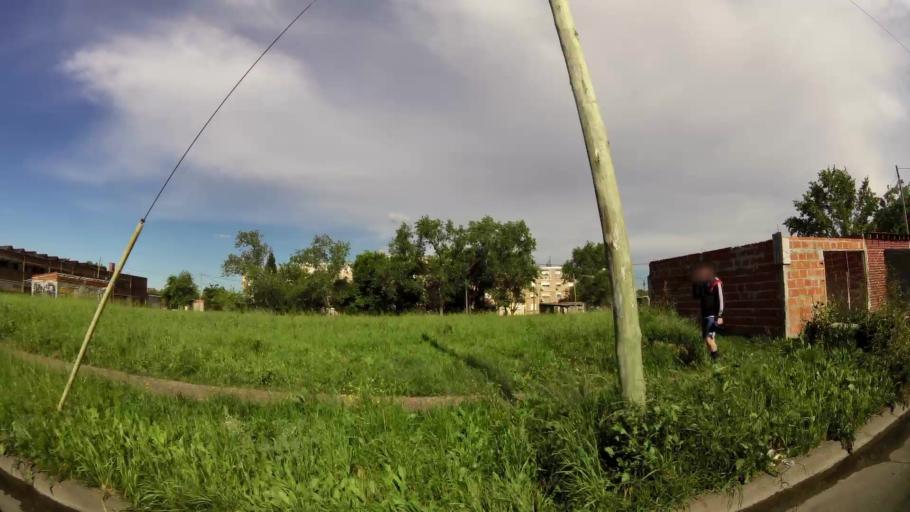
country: AR
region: Buenos Aires
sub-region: Partido de Almirante Brown
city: Adrogue
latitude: -34.8199
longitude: -58.3469
